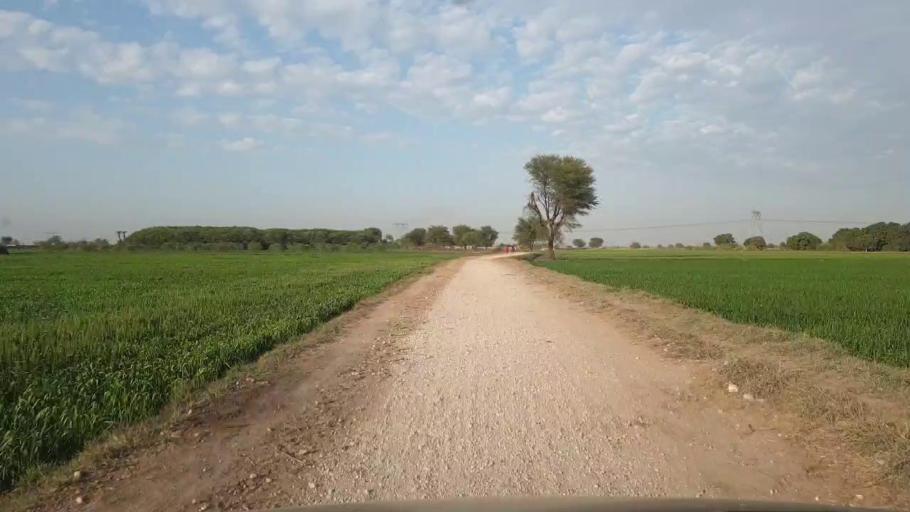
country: PK
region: Sindh
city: Sakrand
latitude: 26.0251
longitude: 68.3678
